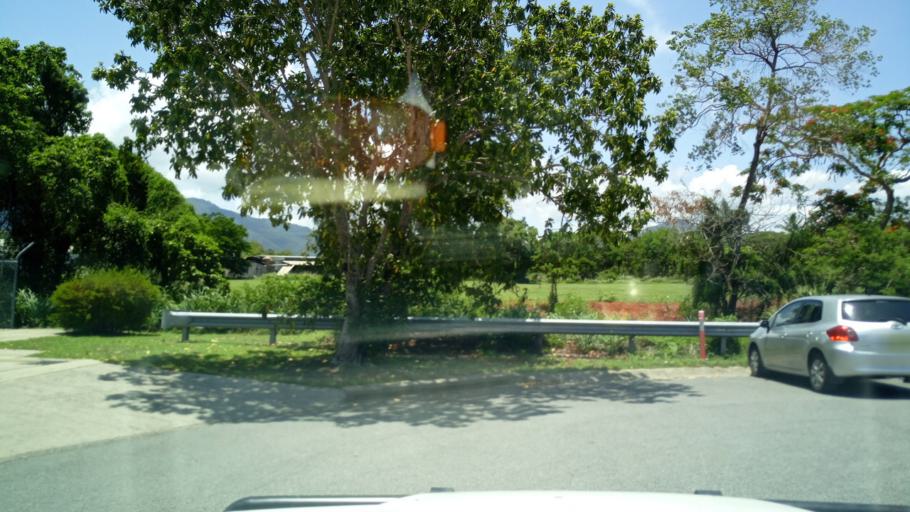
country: AU
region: Queensland
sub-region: Cairns
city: Redlynch
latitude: -16.8727
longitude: 145.7375
